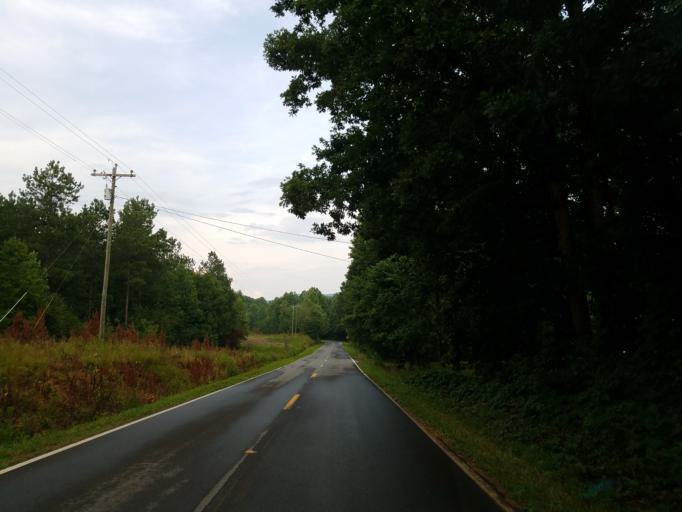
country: US
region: Georgia
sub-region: Pickens County
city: Jasper
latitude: 34.4474
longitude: -84.5690
